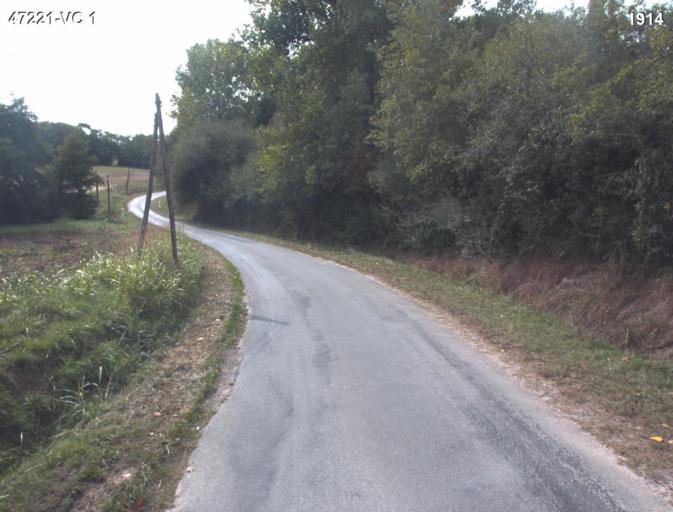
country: FR
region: Aquitaine
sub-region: Departement du Lot-et-Garonne
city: Mezin
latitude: 44.1105
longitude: 0.2398
